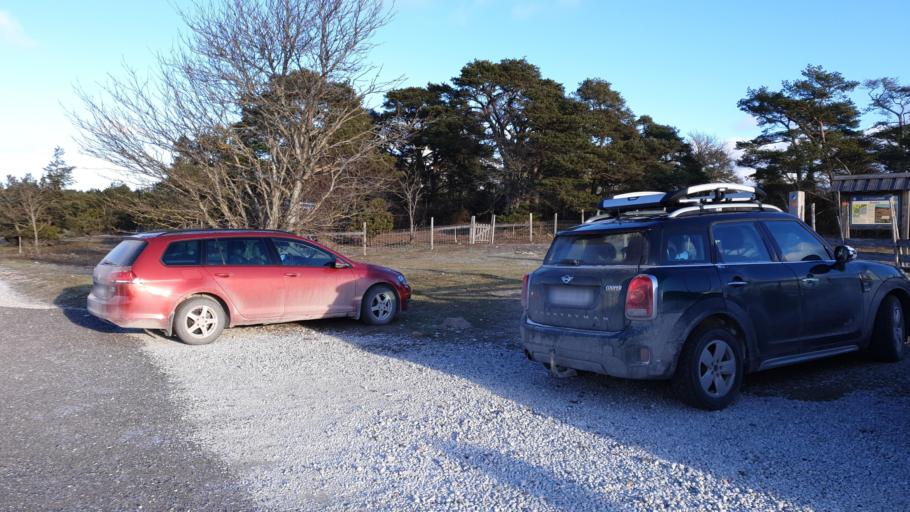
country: SE
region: Gotland
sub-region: Gotland
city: Slite
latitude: 57.3712
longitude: 18.8062
